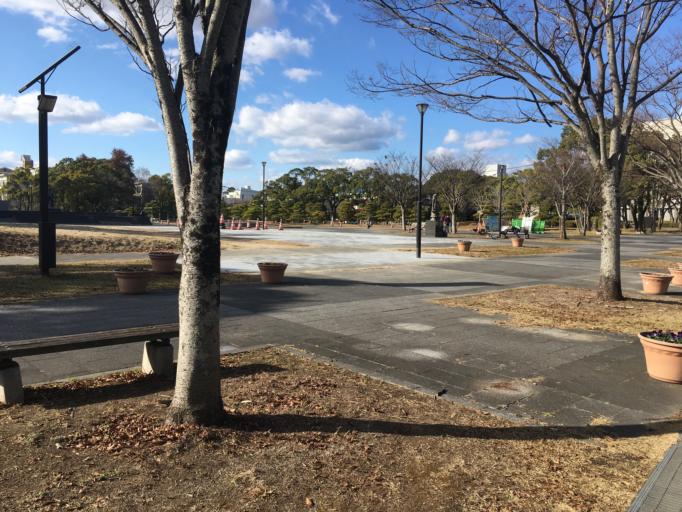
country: JP
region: Saga Prefecture
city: Saga-shi
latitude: 33.2453
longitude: 130.3013
